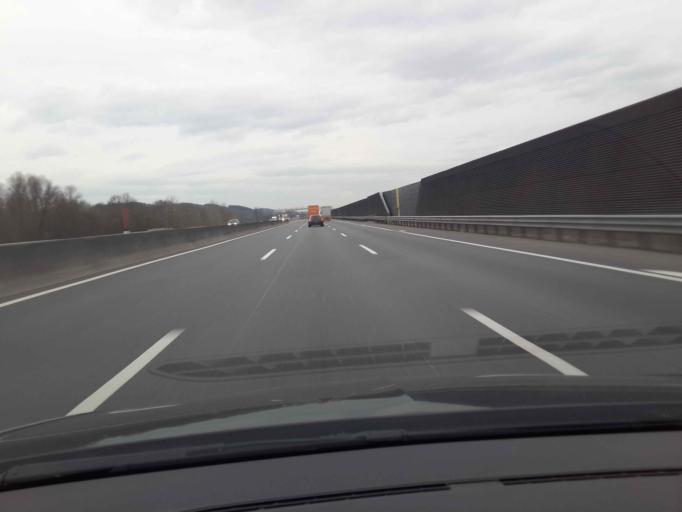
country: AT
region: Lower Austria
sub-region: Politischer Bezirk Melk
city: Neumarkt an der Ybbs
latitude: 48.1412
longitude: 15.0695
